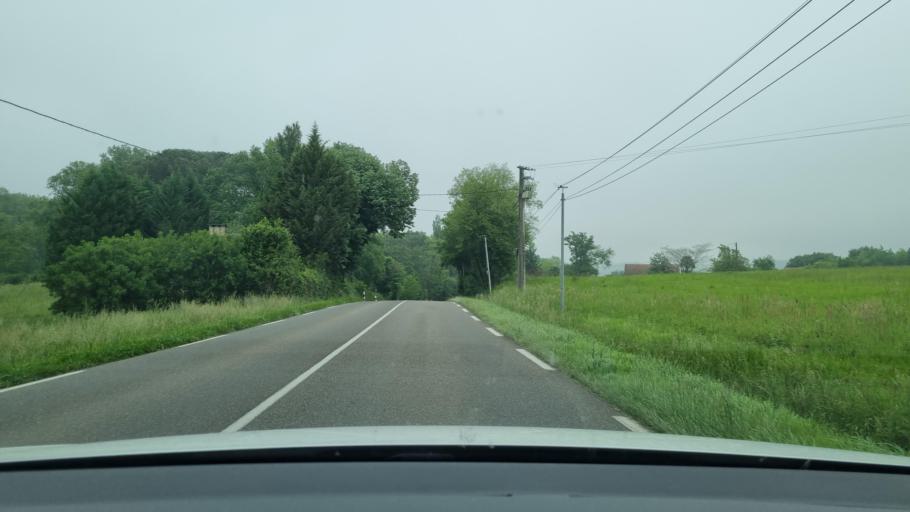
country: FR
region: Aquitaine
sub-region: Departement des Landes
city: Saint-Sever
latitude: 43.7259
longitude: -0.5754
